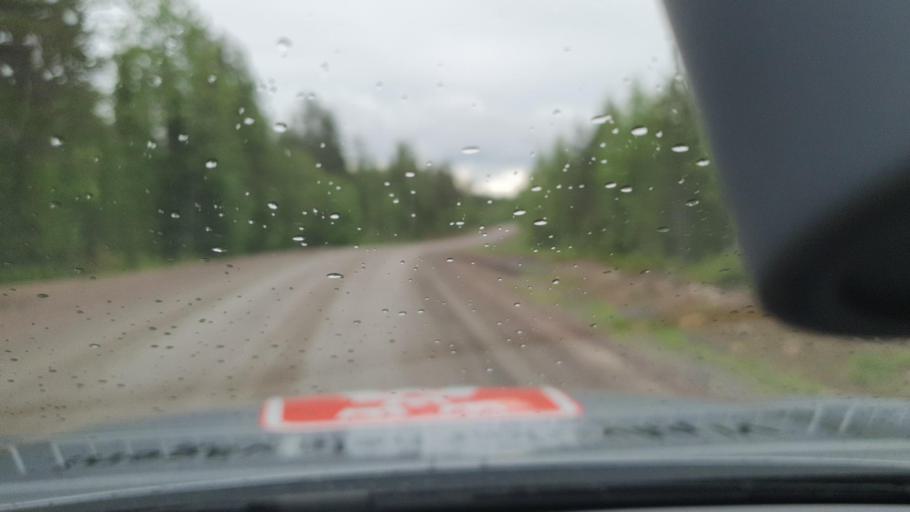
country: SE
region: Norrbotten
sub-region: Overtornea Kommun
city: OEvertornea
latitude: 66.4327
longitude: 23.5176
